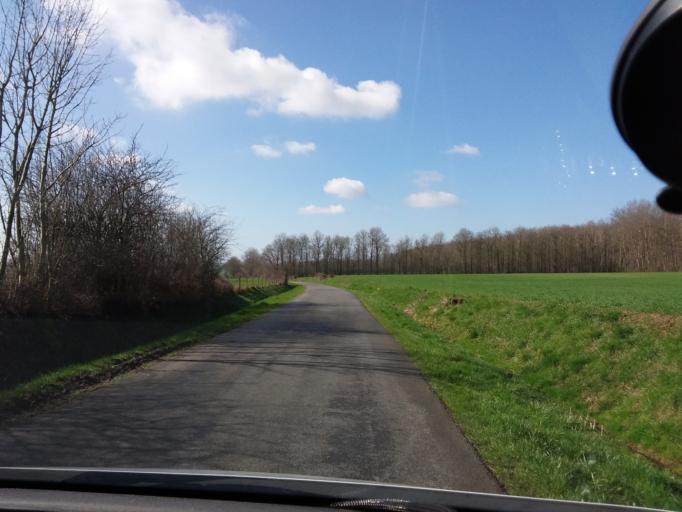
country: FR
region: Picardie
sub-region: Departement de l'Aisne
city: Origny-en-Thierache
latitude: 49.8353
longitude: 4.0572
